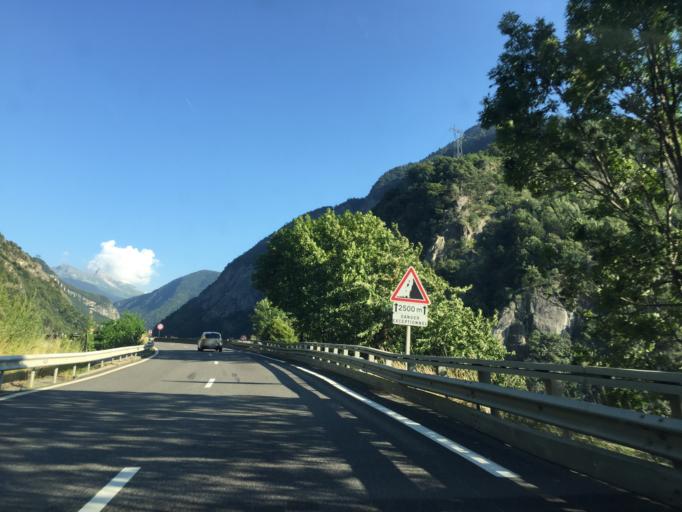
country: FR
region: Rhone-Alpes
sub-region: Departement de la Savoie
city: Aigueblanche
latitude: 45.4982
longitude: 6.5128
